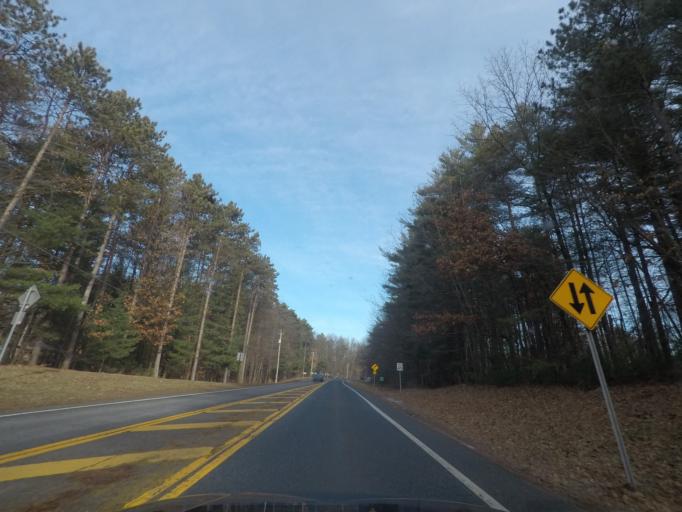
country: US
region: New York
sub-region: Saratoga County
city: Country Knolls
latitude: 42.9734
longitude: -73.7752
